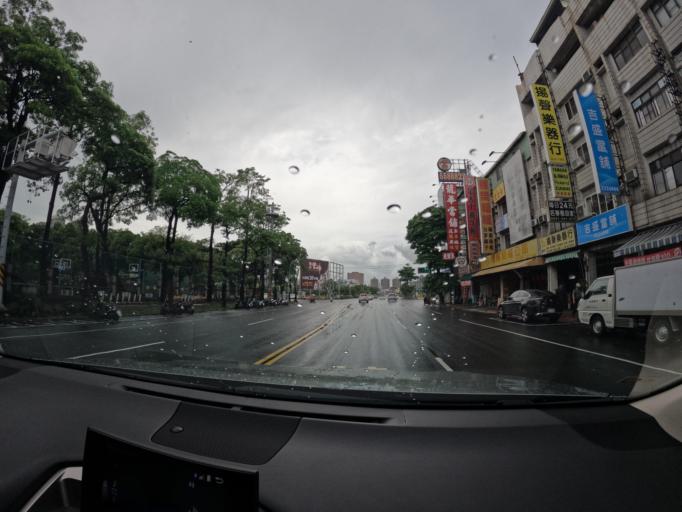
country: TW
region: Kaohsiung
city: Kaohsiung
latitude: 22.6573
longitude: 120.3088
